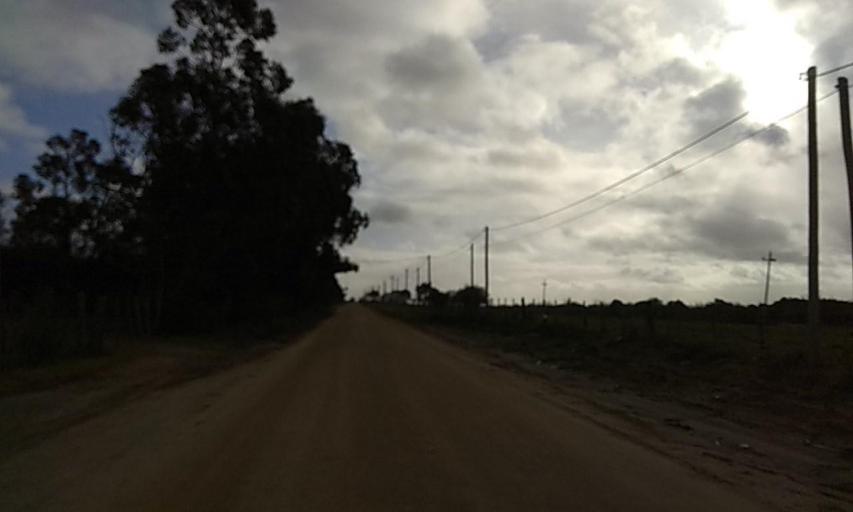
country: UY
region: Florida
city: Florida
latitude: -34.0629
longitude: -56.1930
